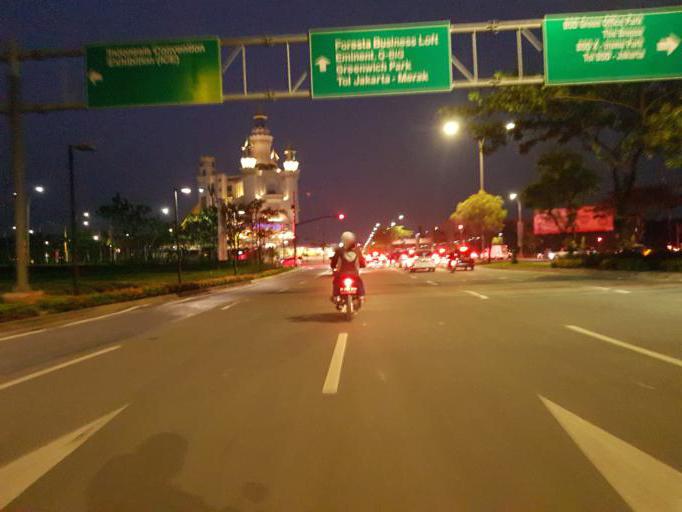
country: ID
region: West Java
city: Serpong
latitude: -6.2997
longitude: 106.6411
